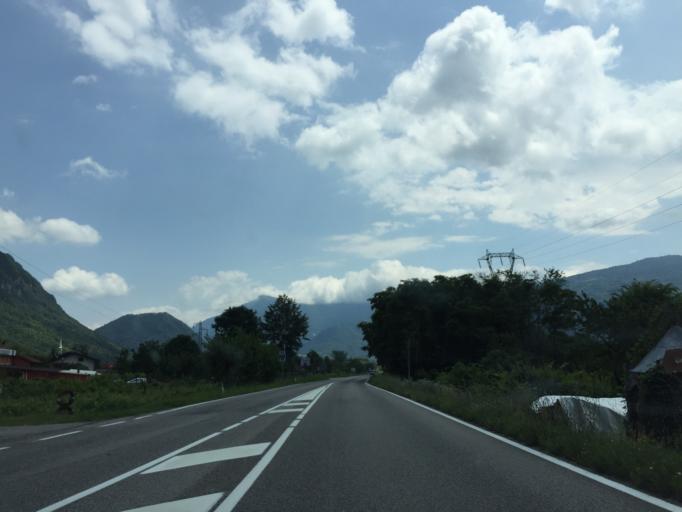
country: IT
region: Veneto
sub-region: Provincia di Belluno
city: Fonzaso
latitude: 46.0205
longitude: 11.7811
